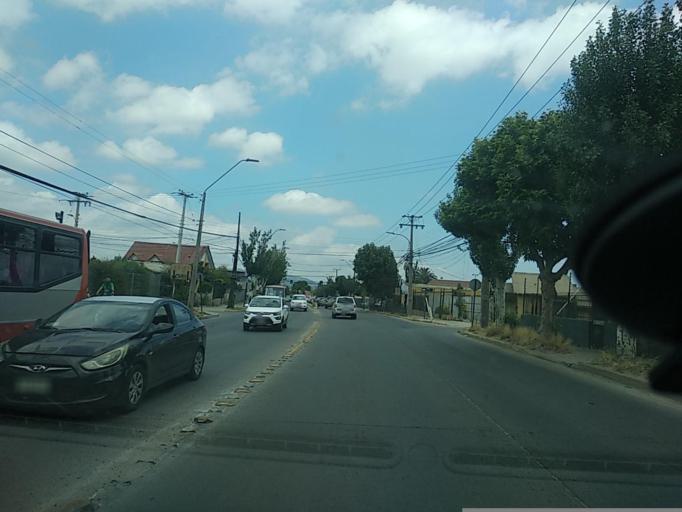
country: CL
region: Valparaiso
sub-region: Provincia de Marga Marga
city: Villa Alemana
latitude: -33.0453
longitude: -71.3894
